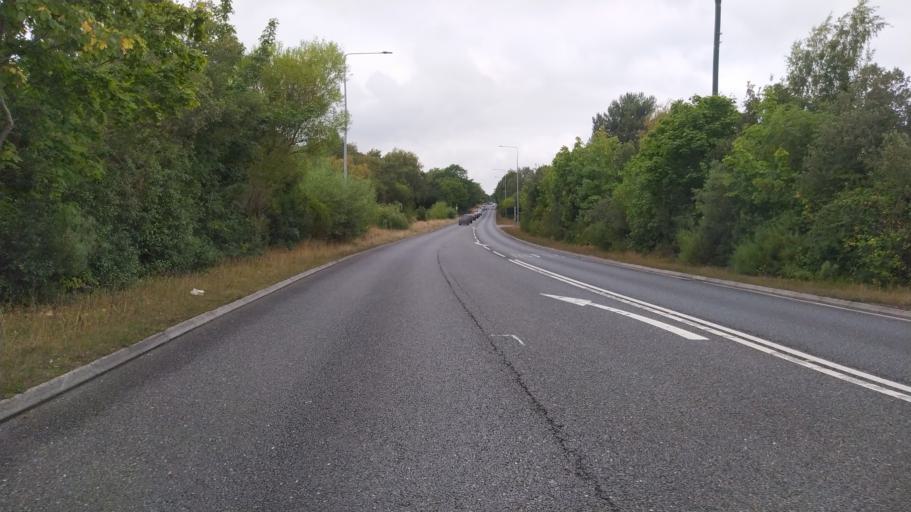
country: GB
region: England
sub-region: Bournemouth
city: Bournemouth
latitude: 50.7226
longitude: -1.8949
